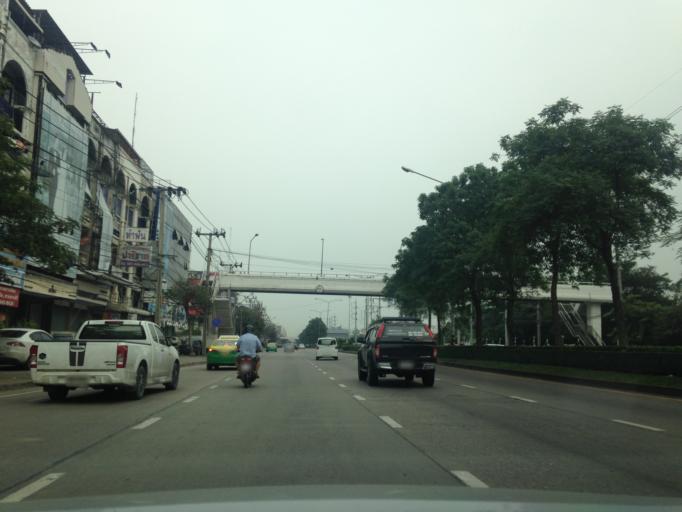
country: TH
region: Bangkok
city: Bang Khen
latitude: 13.8494
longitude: 100.6427
